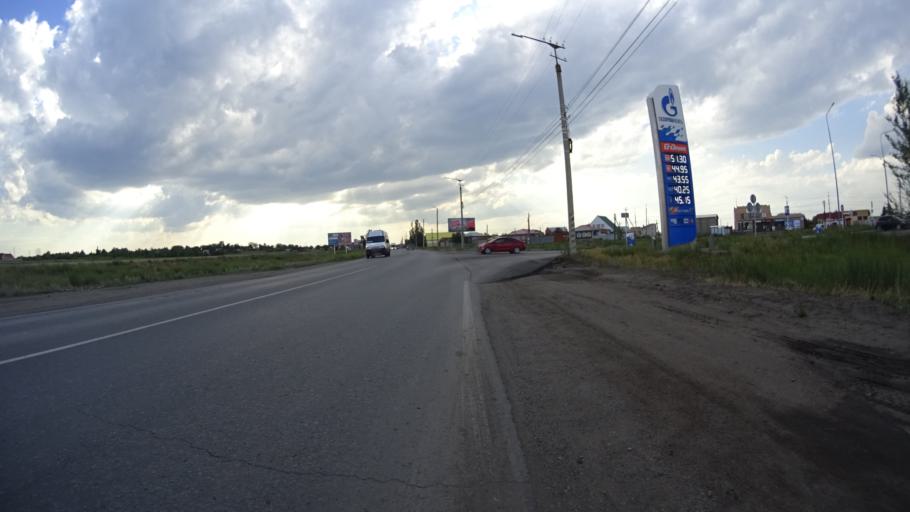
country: RU
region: Chelyabinsk
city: Troitsk
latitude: 54.0822
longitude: 61.5191
